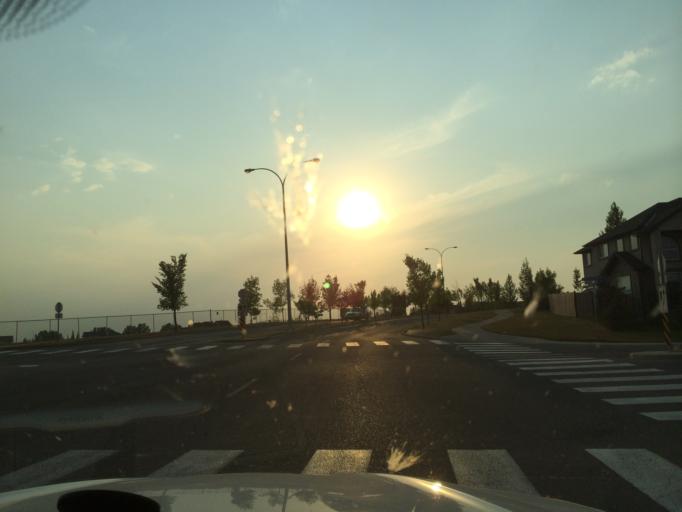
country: CA
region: Alberta
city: Okotoks
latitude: 50.7324
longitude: -113.9546
